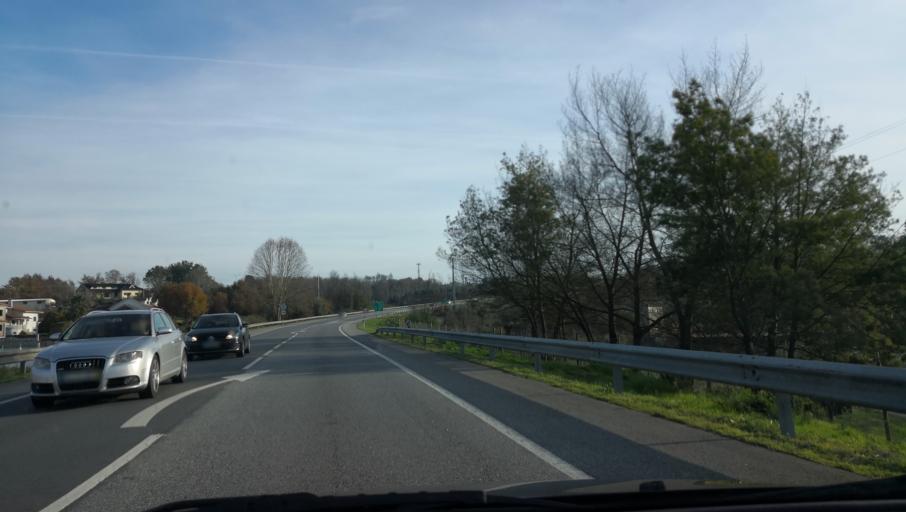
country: PT
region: Viseu
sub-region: Concelho de Tondela
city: Tondela
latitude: 40.5117
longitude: -8.0881
